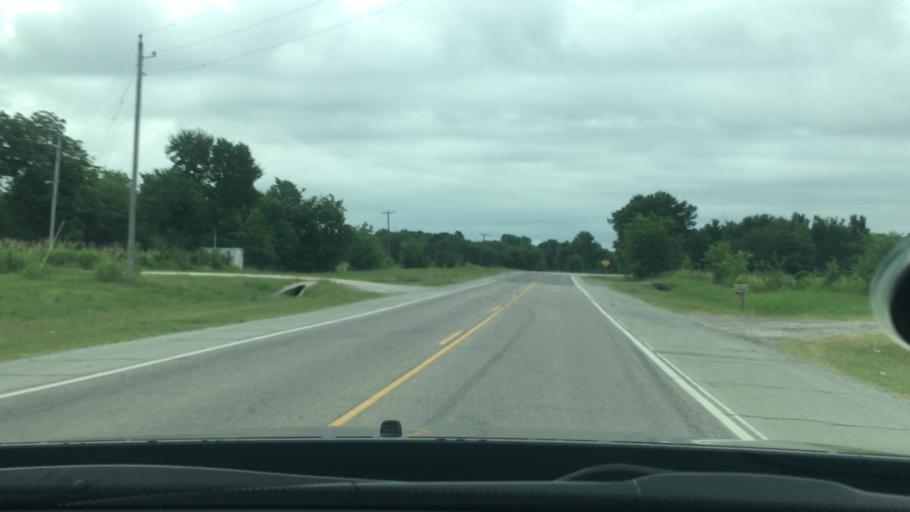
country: US
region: Oklahoma
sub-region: Coal County
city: Coalgate
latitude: 34.5497
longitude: -96.2328
